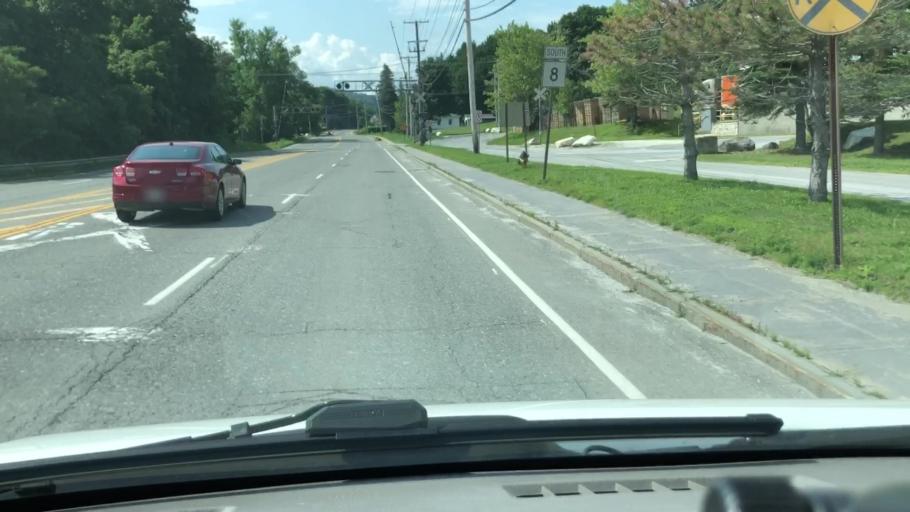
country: US
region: Massachusetts
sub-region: Berkshire County
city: Adams
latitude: 42.6428
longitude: -73.1123
